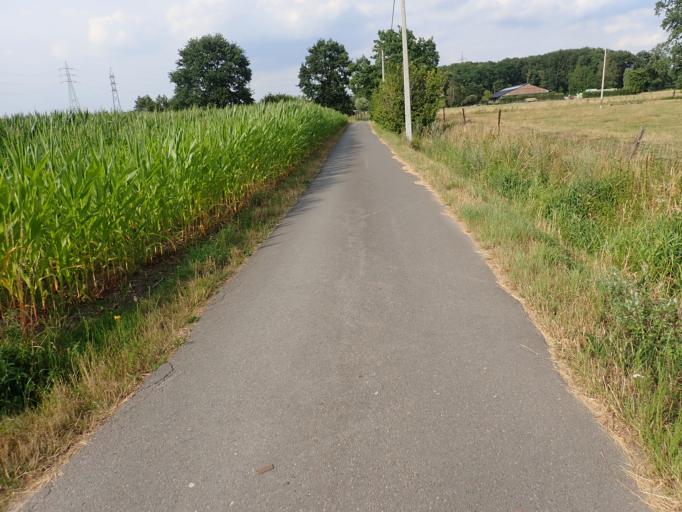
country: BE
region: Flanders
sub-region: Provincie Antwerpen
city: Putte
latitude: 51.0346
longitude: 4.6265
